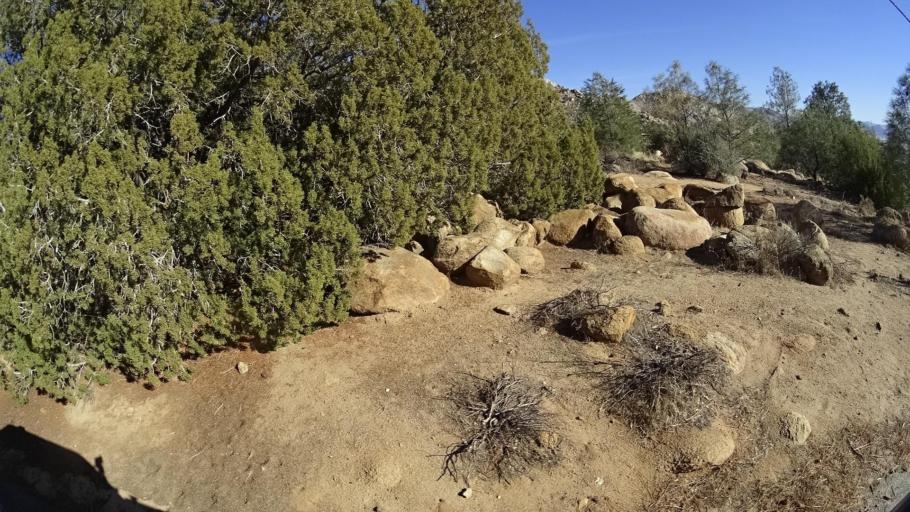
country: US
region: California
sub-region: Kern County
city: Weldon
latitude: 35.7159
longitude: -118.3057
